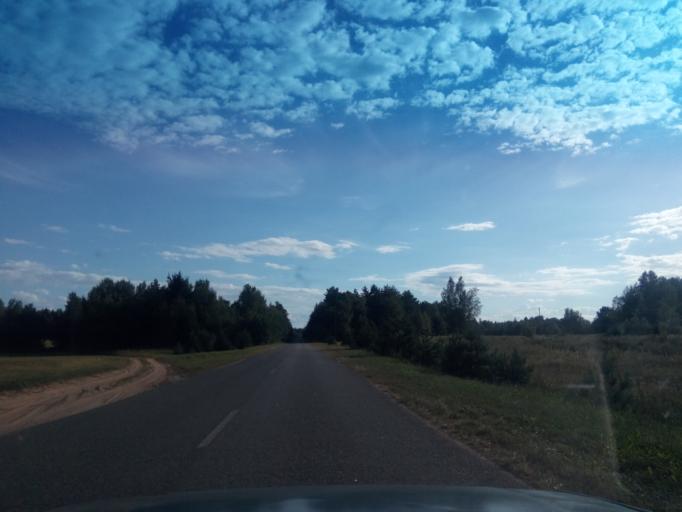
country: BY
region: Vitebsk
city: Polatsk
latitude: 55.4324
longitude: 28.7708
